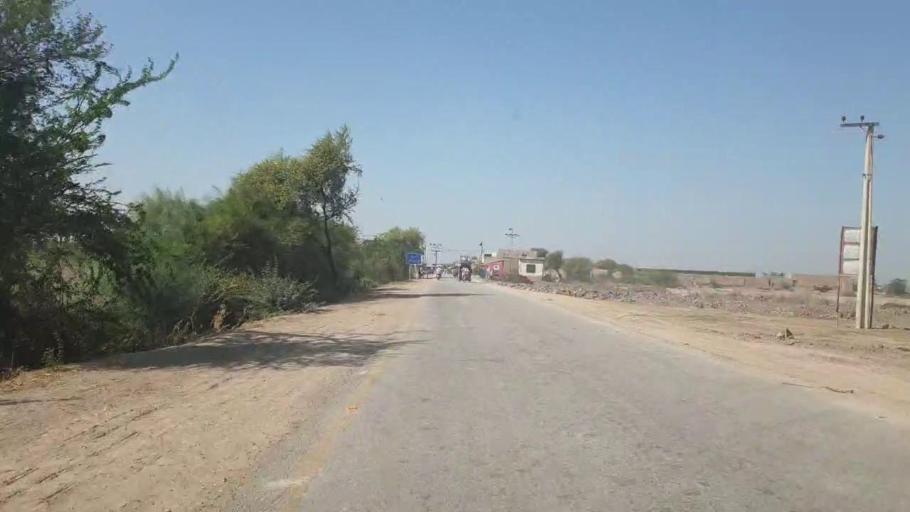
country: PK
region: Sindh
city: Rajo Khanani
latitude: 25.0592
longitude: 68.8014
